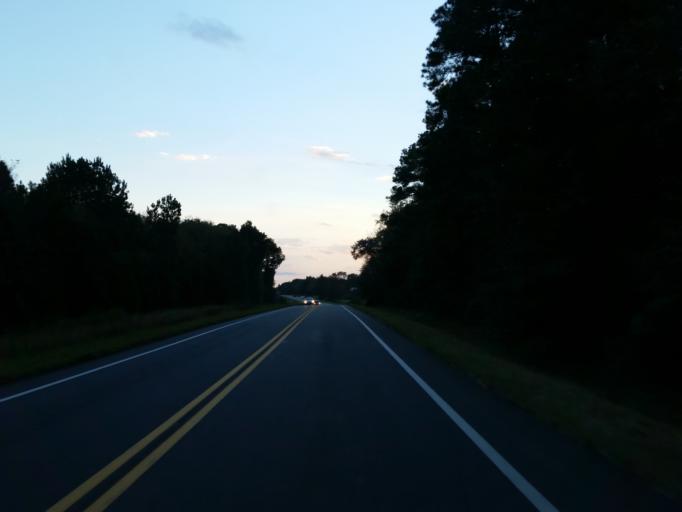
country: US
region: Georgia
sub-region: Pulaski County
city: Hawkinsville
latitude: 32.2559
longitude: -83.4921
